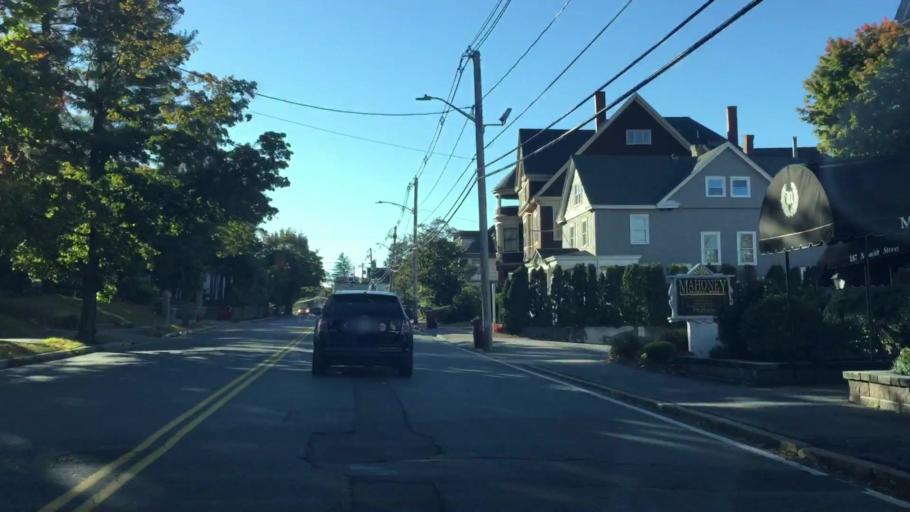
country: US
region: Massachusetts
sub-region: Middlesex County
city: Lowell
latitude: 42.6411
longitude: -71.2969
